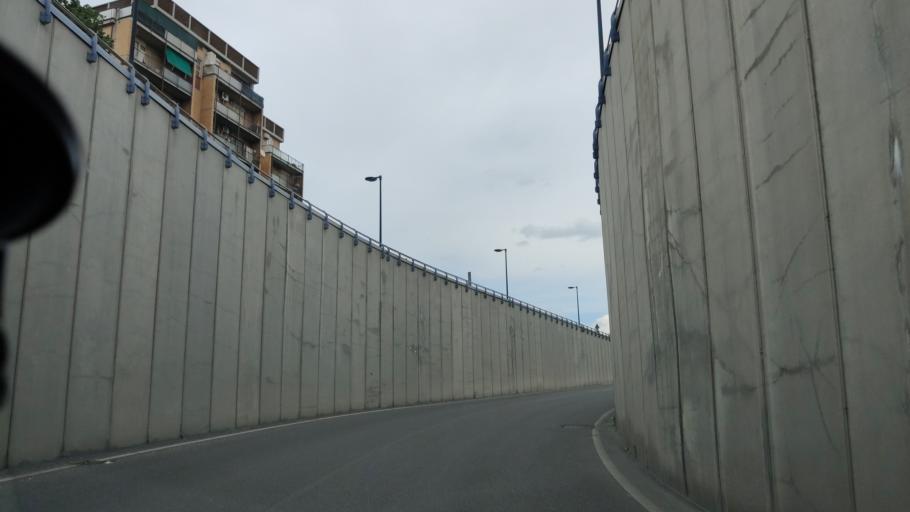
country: IT
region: Umbria
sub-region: Provincia di Terni
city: Terni
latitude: 42.5669
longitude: 12.6598
